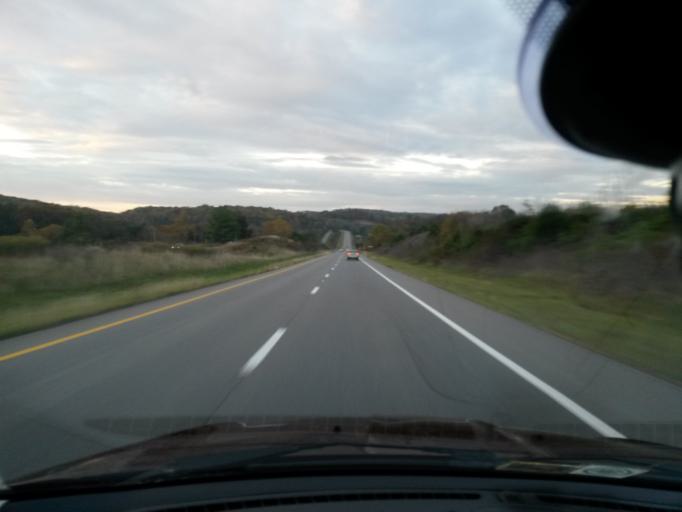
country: US
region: Virginia
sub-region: Botetourt County
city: Fincastle
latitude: 37.6123
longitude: -79.8315
